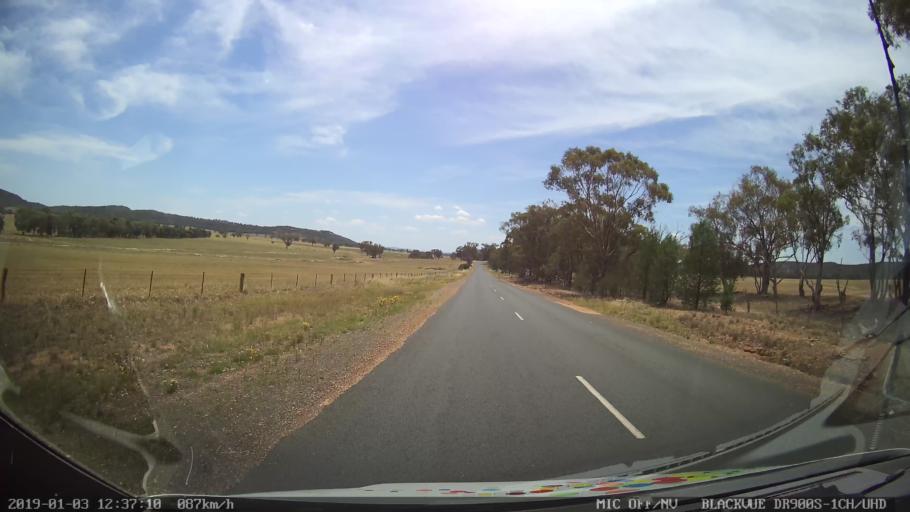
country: AU
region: New South Wales
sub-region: Weddin
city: Grenfell
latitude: -33.8457
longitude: 148.1816
